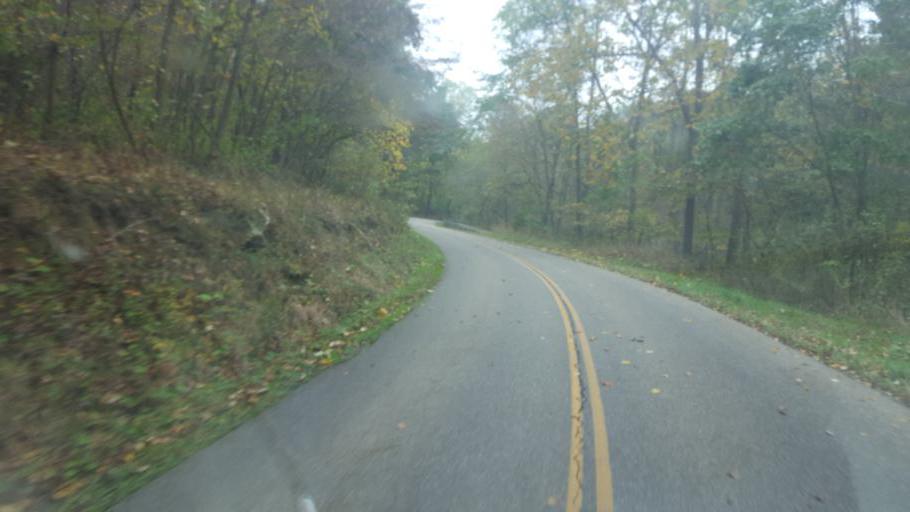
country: US
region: Ohio
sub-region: Carroll County
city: Carrollton
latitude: 40.5304
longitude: -81.1378
